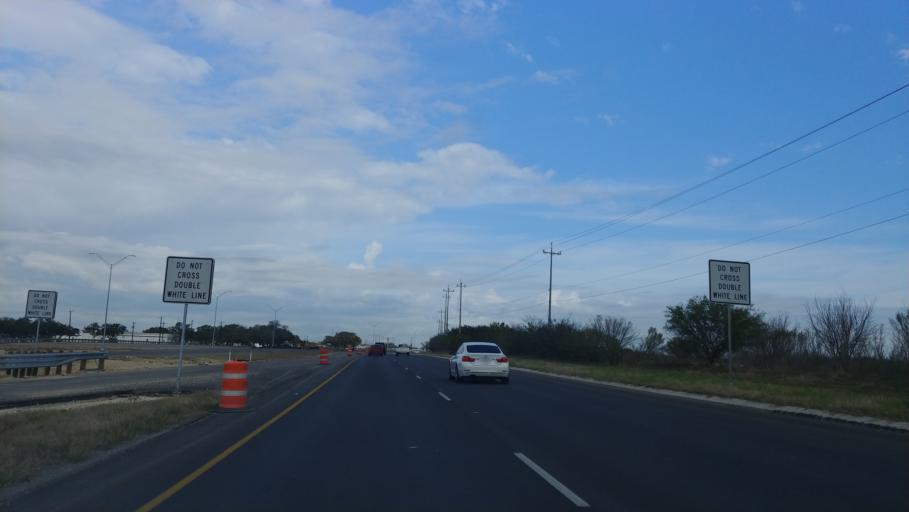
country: US
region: Texas
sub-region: Bexar County
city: Lackland Air Force Base
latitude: 29.4231
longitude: -98.7096
